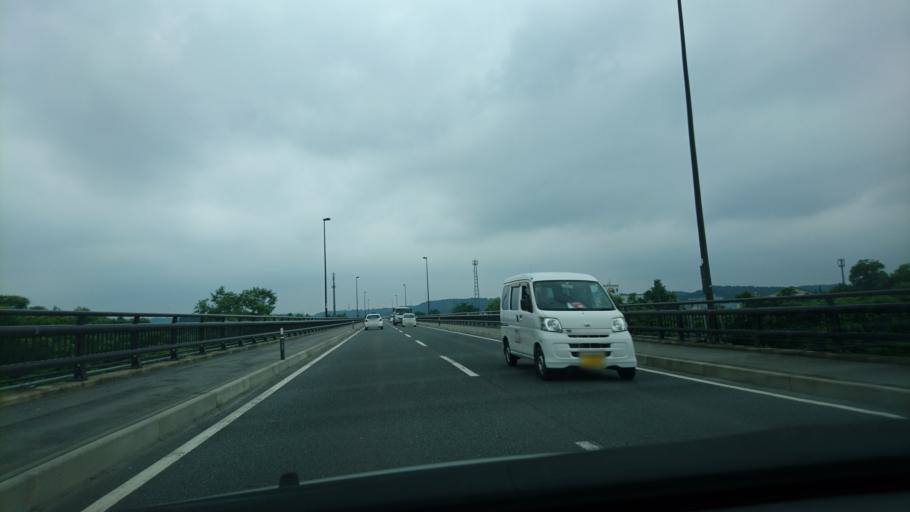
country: JP
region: Miyagi
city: Furukawa
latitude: 38.6548
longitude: 140.8801
